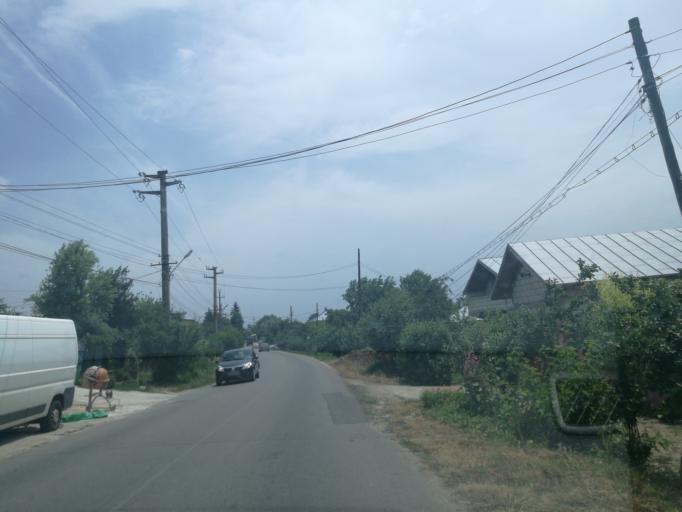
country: RO
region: Ilfov
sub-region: Comuna Vidra
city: Sintesti
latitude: 44.2936
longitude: 26.1271
